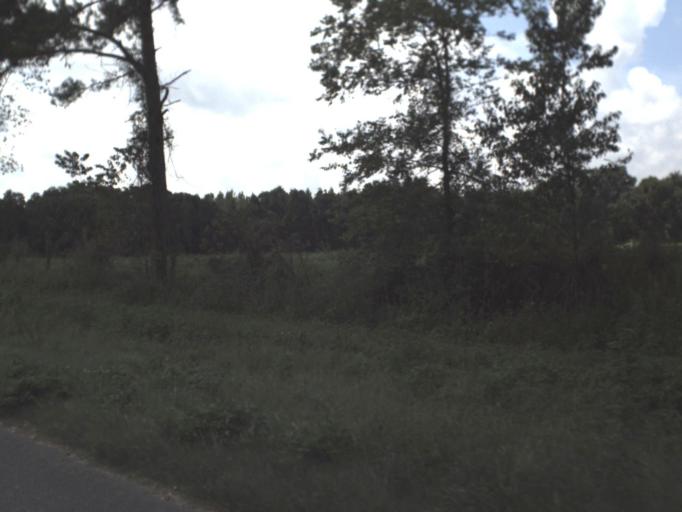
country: US
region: Florida
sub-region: Gilchrist County
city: Trenton
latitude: 29.6416
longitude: -82.8325
